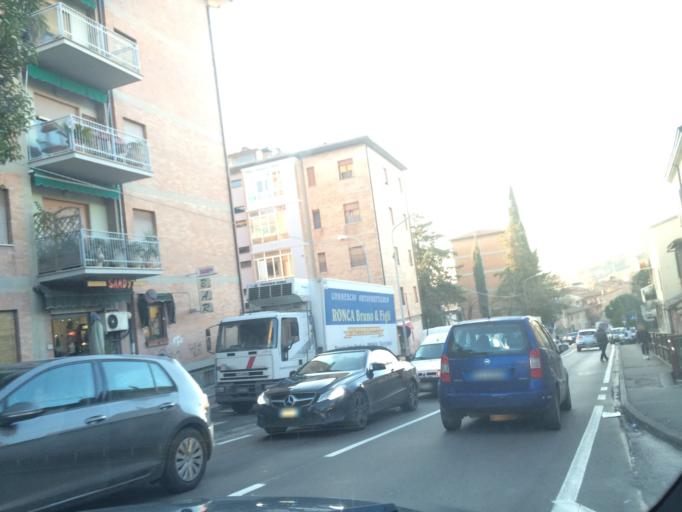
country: IT
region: Umbria
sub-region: Provincia di Perugia
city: Perugia
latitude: 43.1000
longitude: 12.3867
